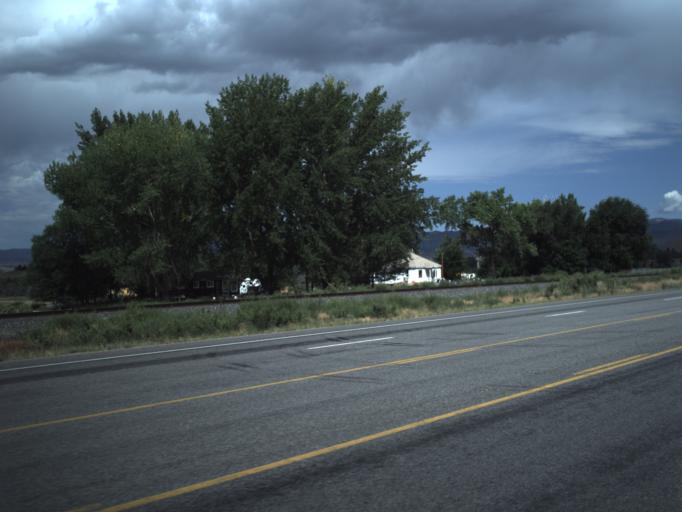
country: US
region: Utah
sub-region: Carbon County
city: Price
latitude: 39.5765
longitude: -110.7849
